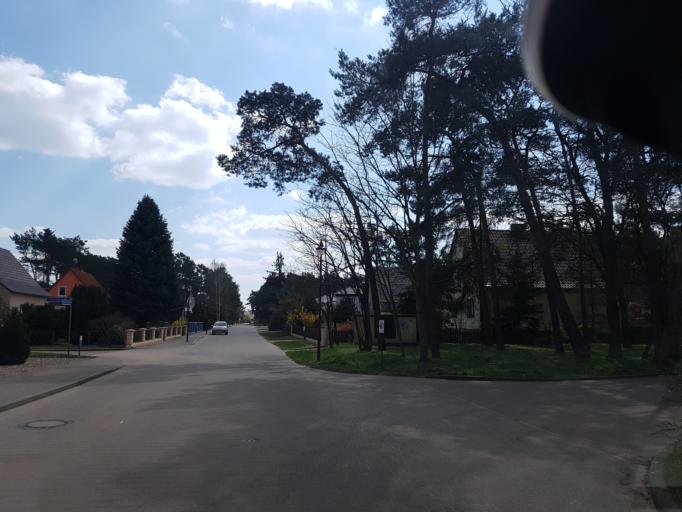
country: DE
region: Brandenburg
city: Bruck
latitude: 52.1822
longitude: 12.7603
